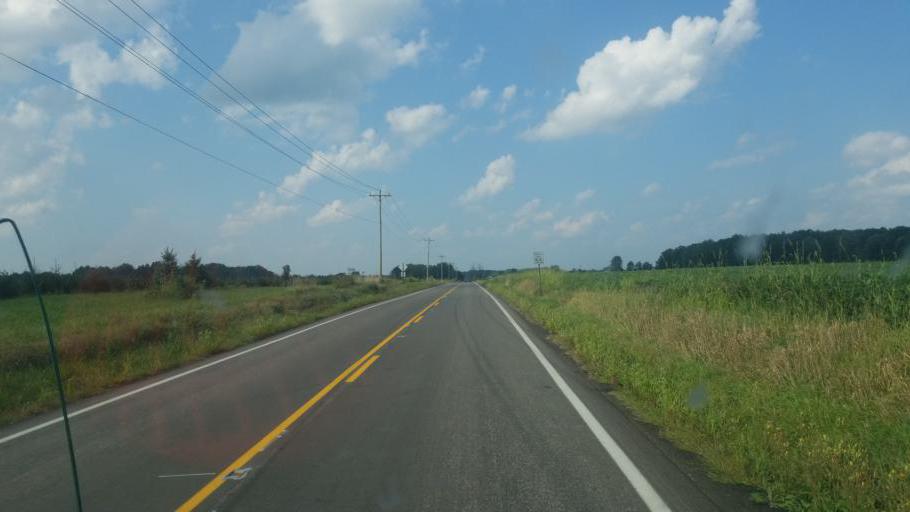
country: US
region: Ohio
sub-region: Wayne County
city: West Salem
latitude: 40.9529
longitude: -82.0846
